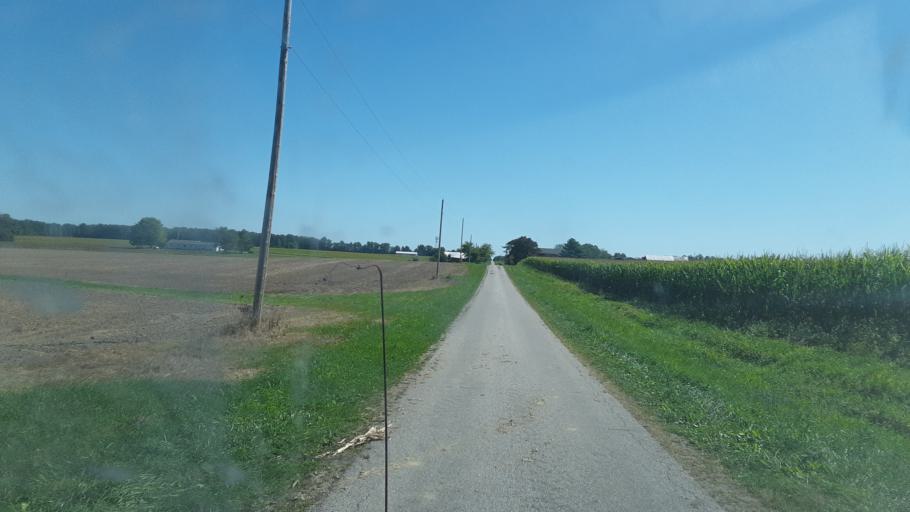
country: US
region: Ohio
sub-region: Sandusky County
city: Mount Carmel
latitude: 41.1467
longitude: -82.9432
